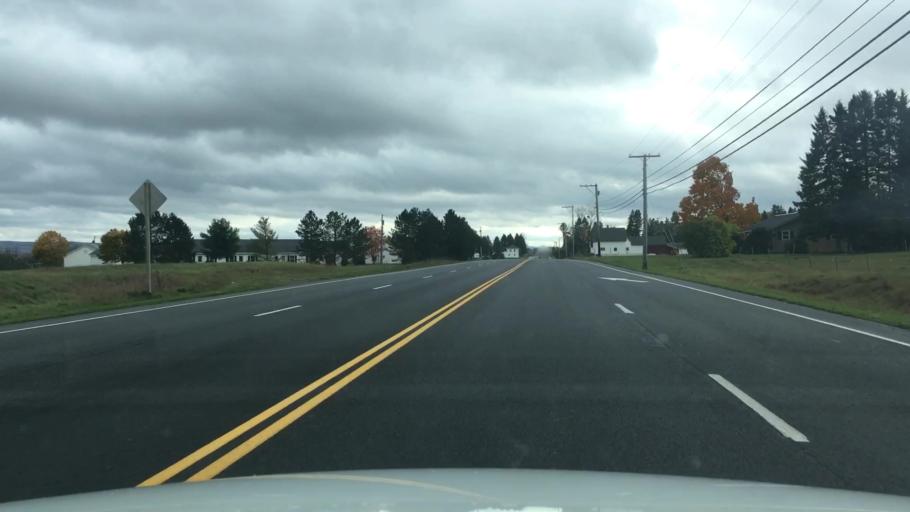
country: US
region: Maine
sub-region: Aroostook County
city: Houlton
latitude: 46.2276
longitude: -67.8410
